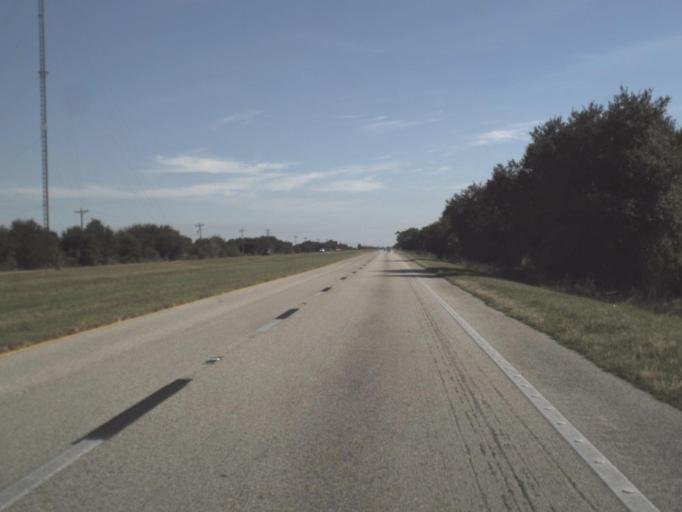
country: US
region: Florida
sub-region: Glades County
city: Moore Haven
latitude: 26.8702
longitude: -81.2194
